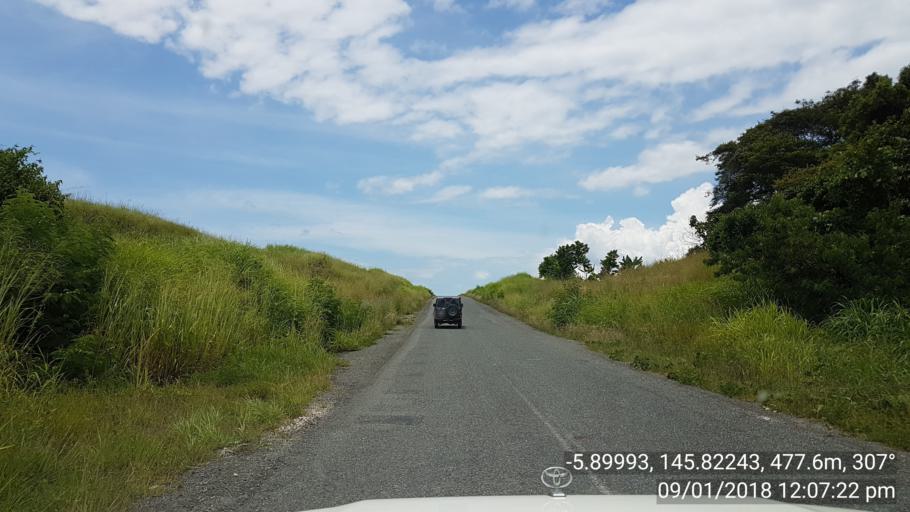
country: PG
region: Eastern Highlands
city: Kainantu
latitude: -5.9000
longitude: 145.8225
